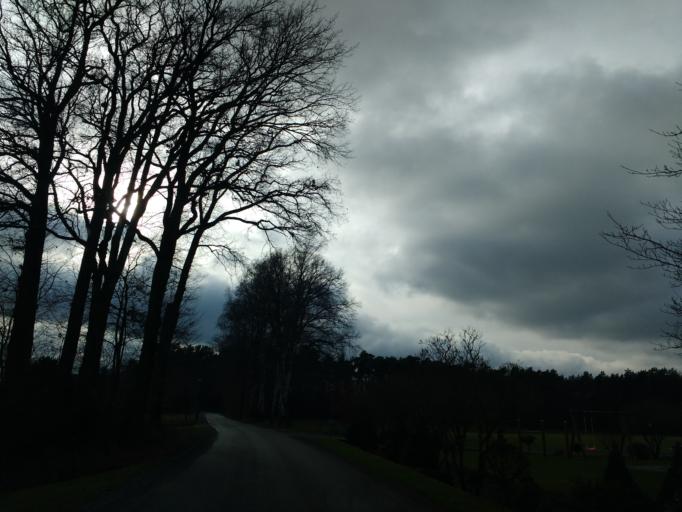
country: DE
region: North Rhine-Westphalia
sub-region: Regierungsbezirk Detmold
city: Hovelhof
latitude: 51.8363
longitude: 8.6762
